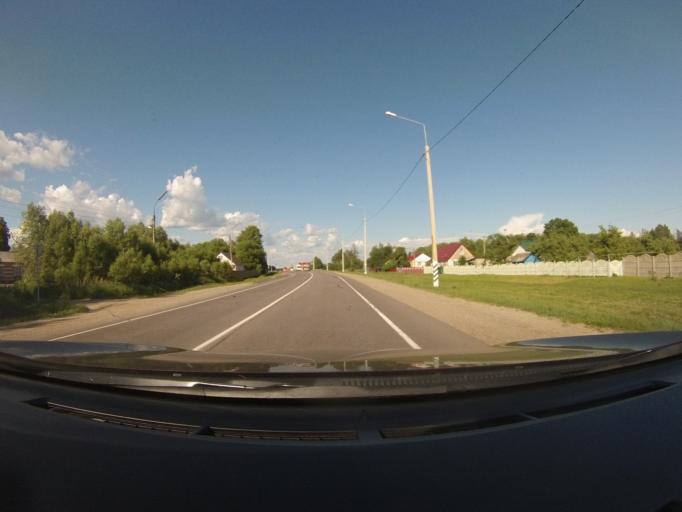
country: RU
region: Tula
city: Bol'shoye Skuratovo
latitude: 53.3956
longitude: 36.7561
